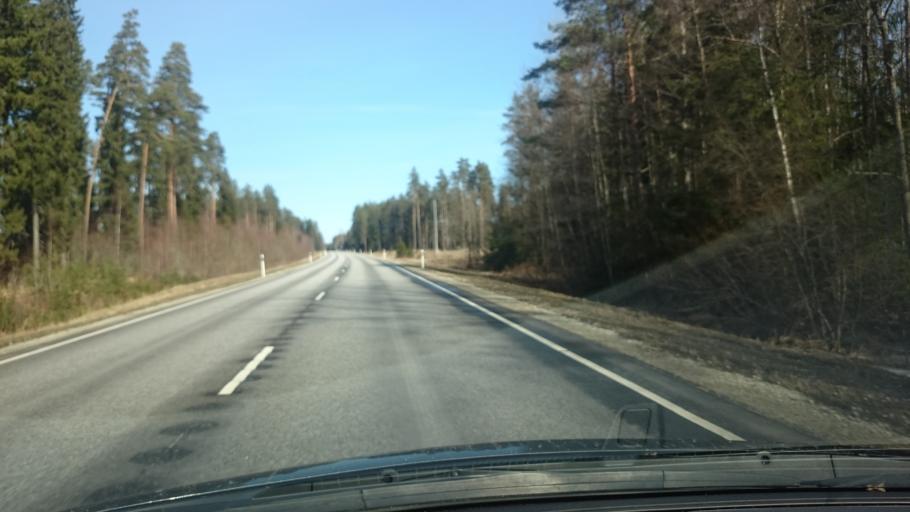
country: EE
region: Paernumaa
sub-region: Vaendra vald (alev)
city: Vandra
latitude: 58.6851
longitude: 25.2393
